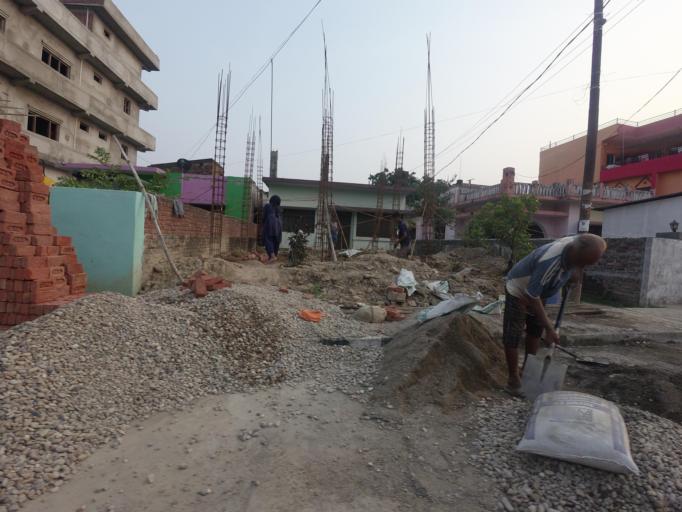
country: NP
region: Western Region
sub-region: Lumbini Zone
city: Bhairahawa
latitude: 27.5139
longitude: 83.4486
